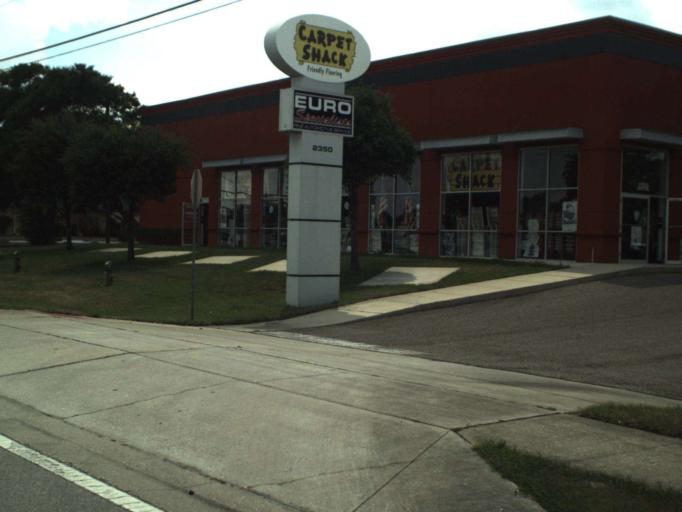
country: US
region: Florida
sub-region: Seminole County
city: Casselberry
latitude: 28.6847
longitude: -81.3336
